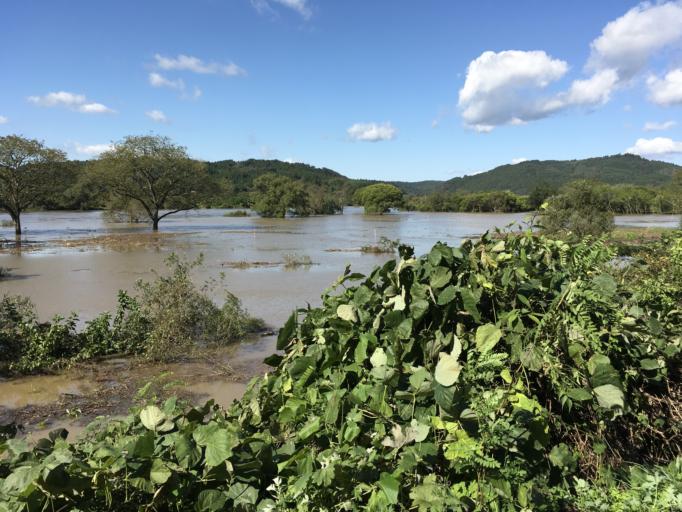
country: JP
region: Iwate
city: Ichinoseki
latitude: 38.8307
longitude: 141.2624
